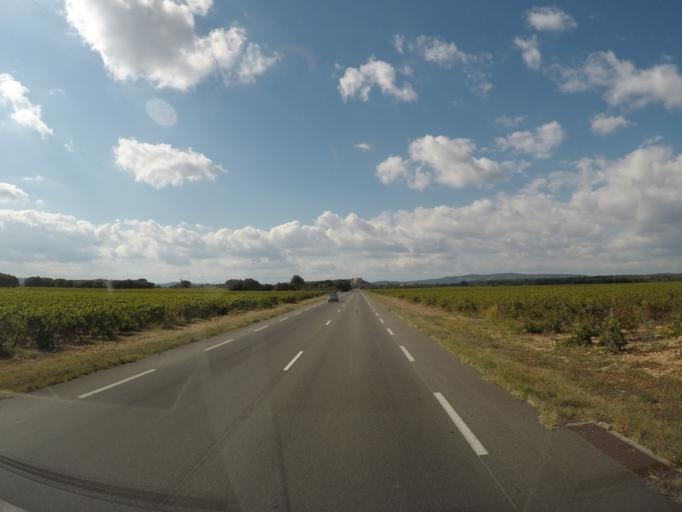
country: FR
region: Rhone-Alpes
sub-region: Departement de la Drome
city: Suze-la-Rousse
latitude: 44.2871
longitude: 4.8603
